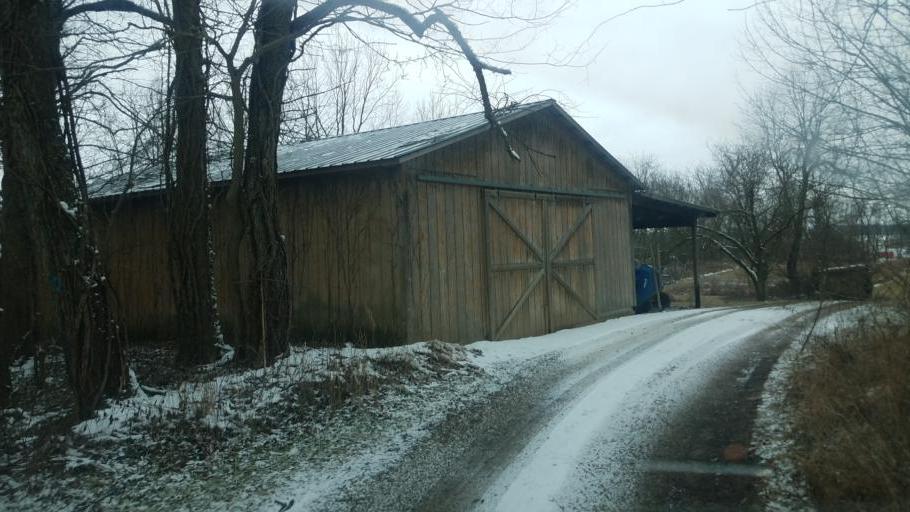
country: US
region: Ohio
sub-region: Knox County
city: Fredericktown
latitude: 40.4667
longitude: -82.6375
